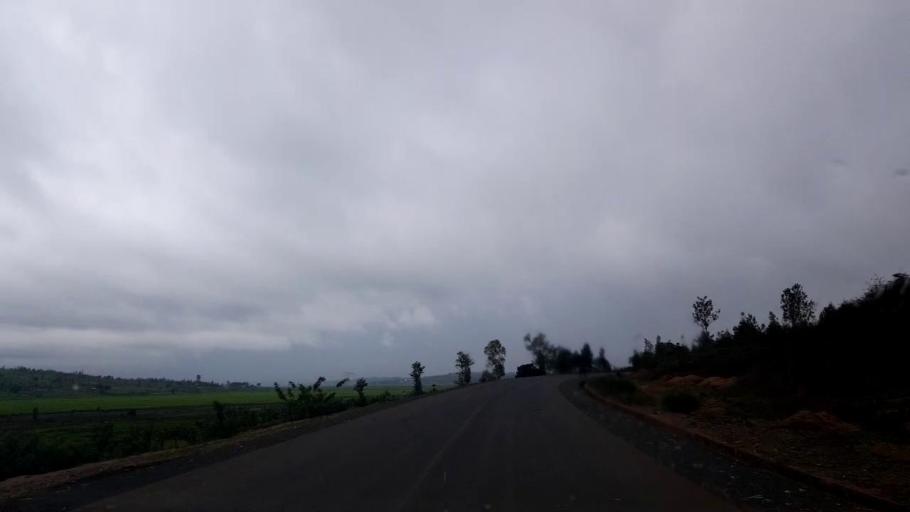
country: RW
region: Northern Province
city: Byumba
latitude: -1.4250
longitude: 30.2675
